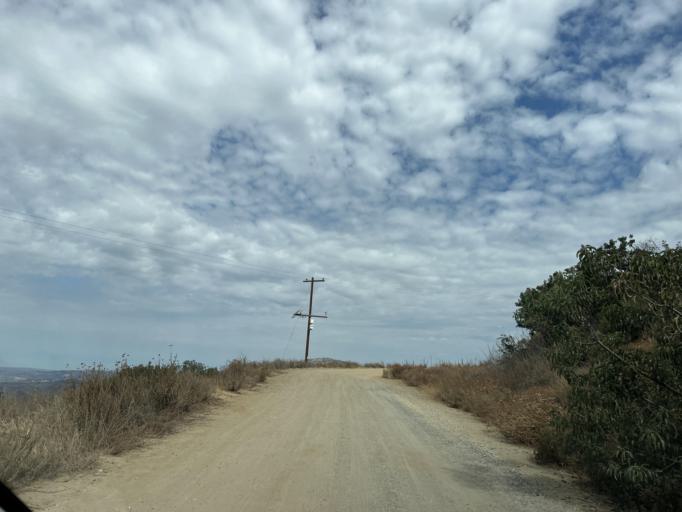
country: US
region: California
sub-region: San Diego County
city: Alpine
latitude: 32.8536
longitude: -116.7419
